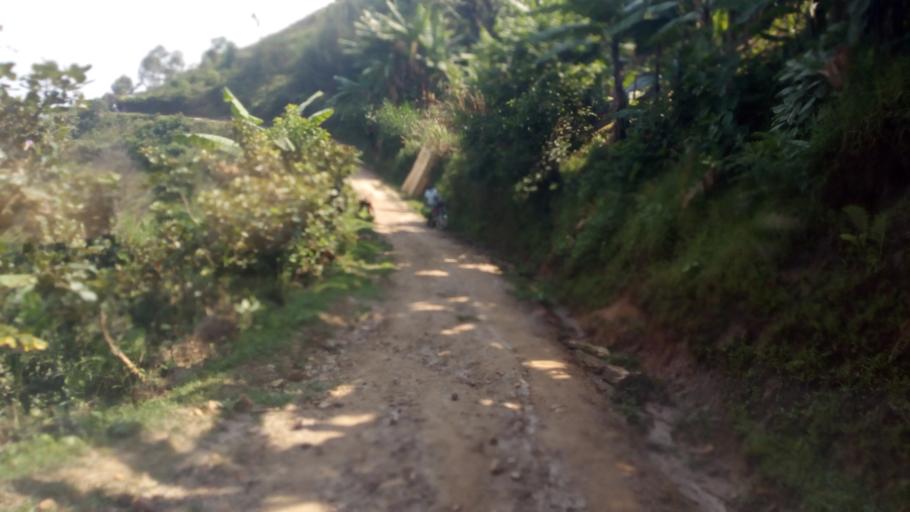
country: UG
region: Western Region
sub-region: Kisoro District
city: Kisoro
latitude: -1.1020
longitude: 29.5880
